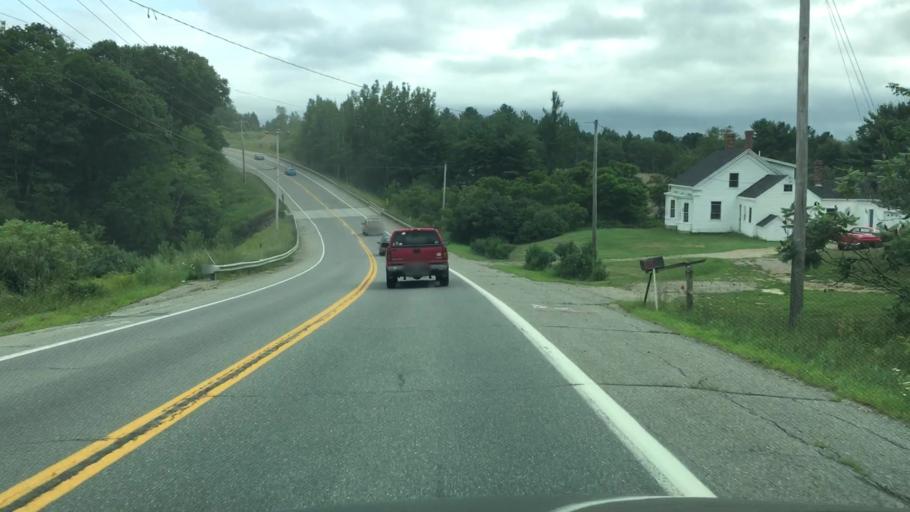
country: US
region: Maine
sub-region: Waldo County
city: Frankfort
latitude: 44.5594
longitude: -68.8662
